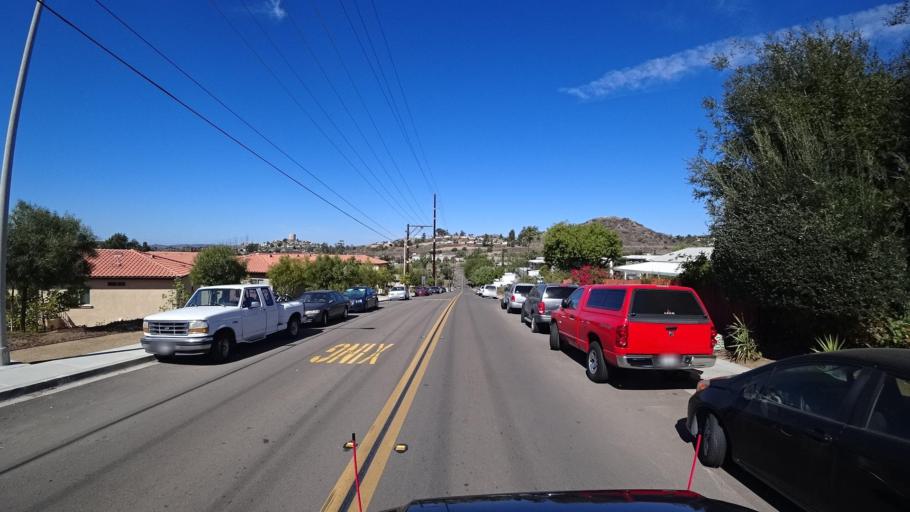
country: US
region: California
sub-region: San Diego County
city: Crest
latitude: 32.8410
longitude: -116.8761
